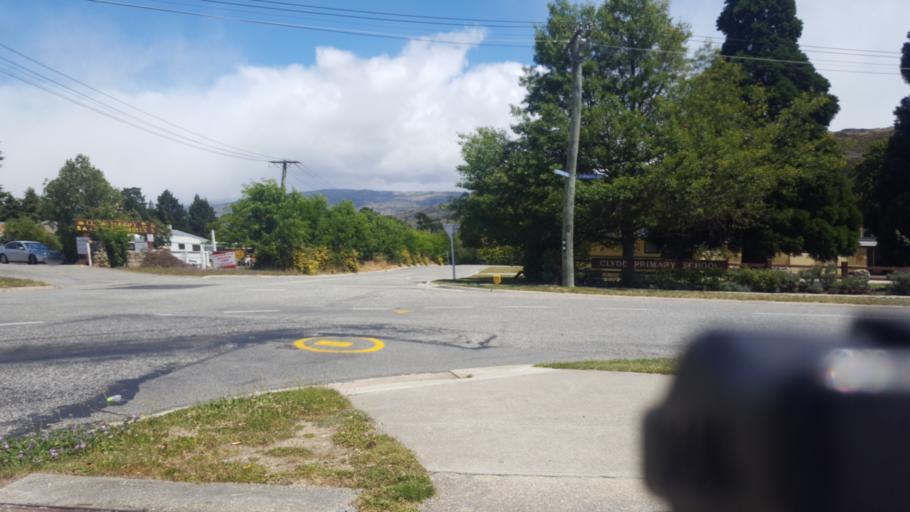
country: NZ
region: Otago
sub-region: Queenstown-Lakes District
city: Wanaka
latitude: -45.1912
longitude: 169.3202
